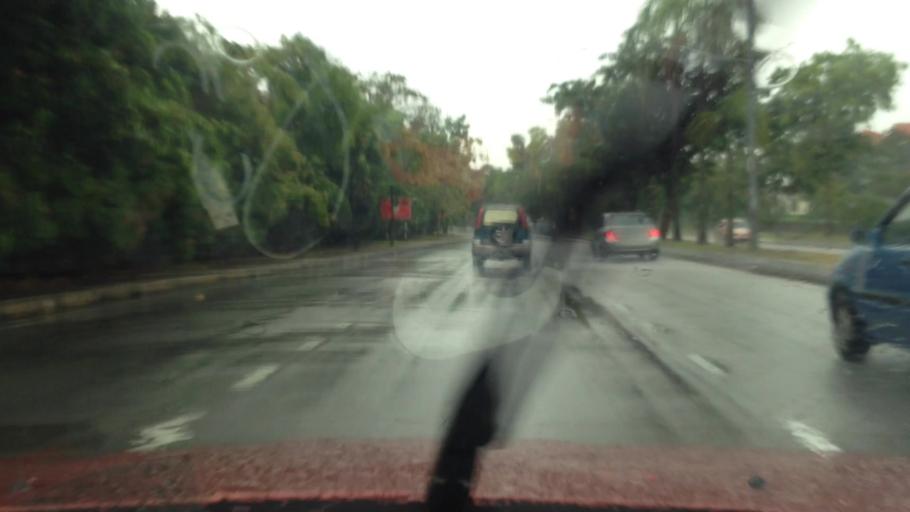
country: MY
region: Selangor
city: Subang Jaya
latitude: 3.0575
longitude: 101.5715
